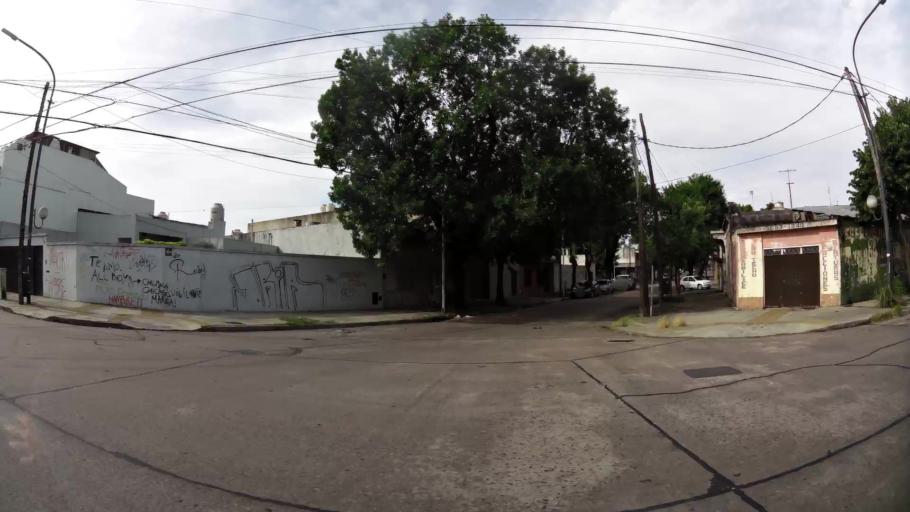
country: AR
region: Buenos Aires F.D.
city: Villa Lugano
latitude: -34.6533
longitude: -58.4832
